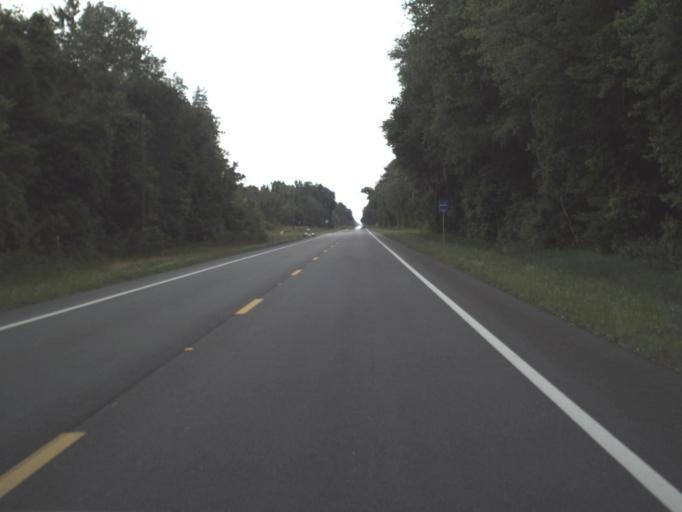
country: US
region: Florida
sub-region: Columbia County
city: Five Points
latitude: 30.4543
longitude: -82.6500
